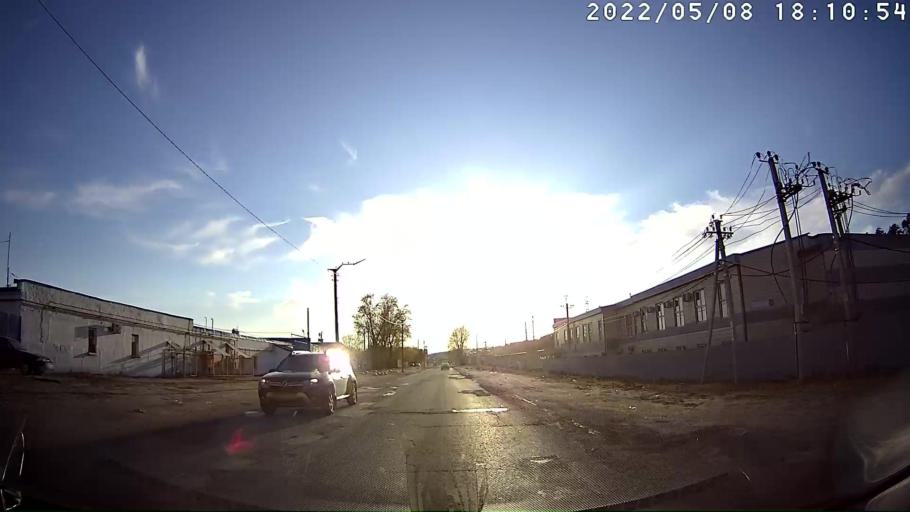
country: RU
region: Tatarstan
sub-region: Zelenodol'skiy Rayon
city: Zelenodolsk
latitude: 55.8397
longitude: 48.5184
